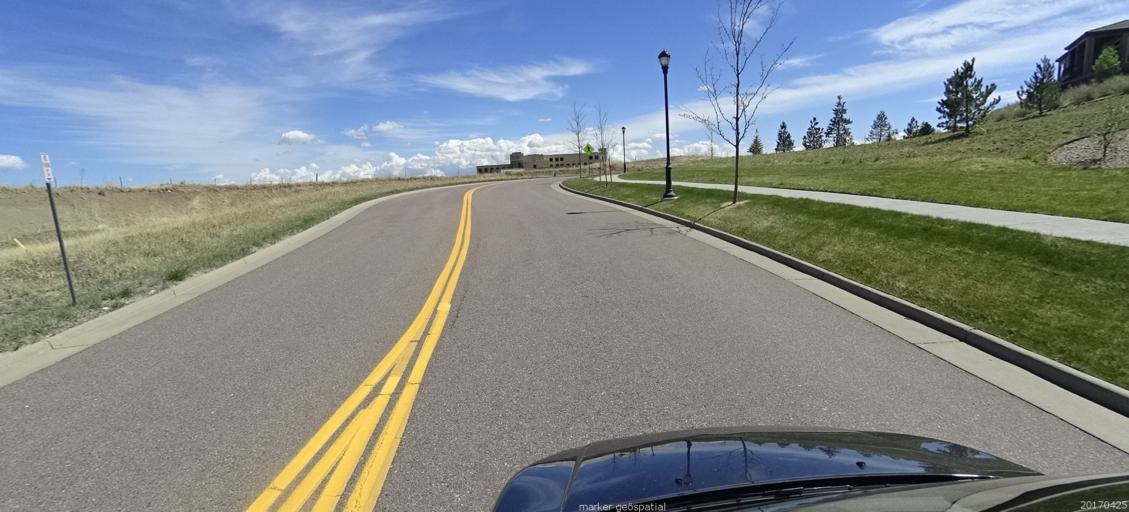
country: US
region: Colorado
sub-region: Douglas County
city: Carriage Club
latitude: 39.5268
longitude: -104.8755
